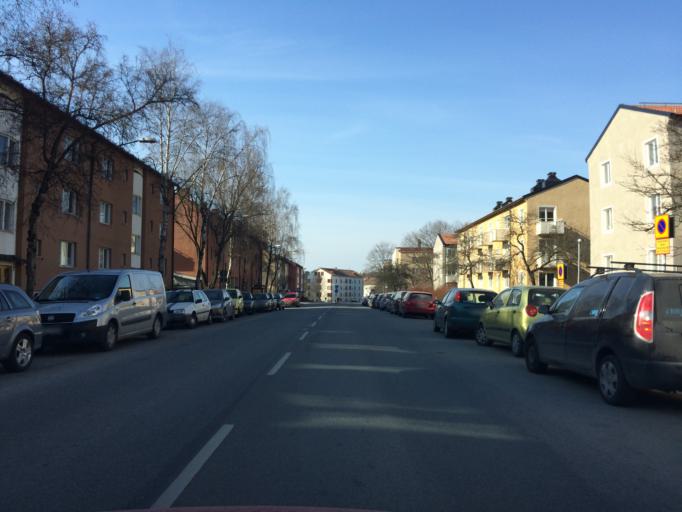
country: SE
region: Stockholm
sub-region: Stockholms Kommun
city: Arsta
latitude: 59.2993
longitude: 18.0441
